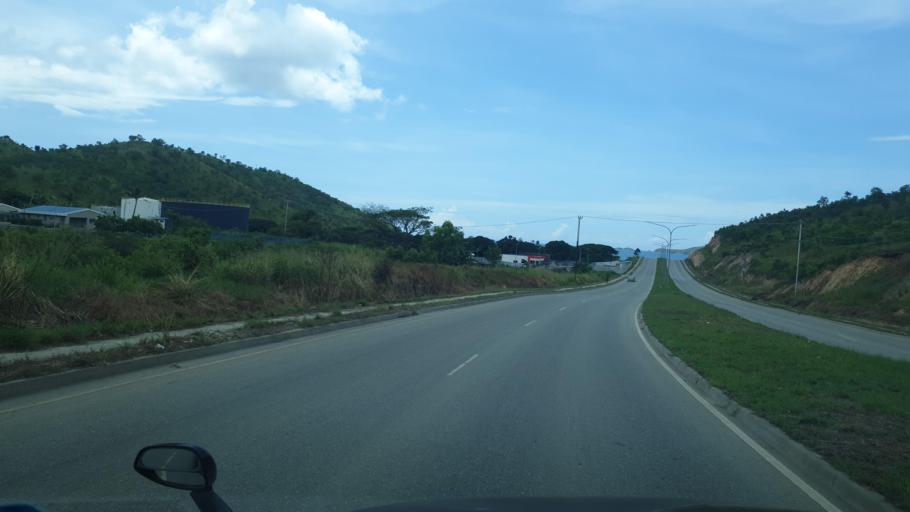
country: PG
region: National Capital
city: Port Moresby
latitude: -9.4310
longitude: 147.1413
